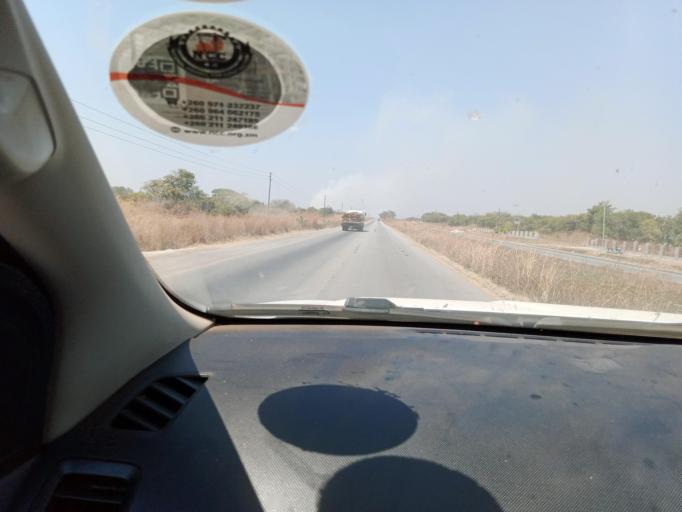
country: ZM
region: Copperbelt
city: Kitwe
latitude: -12.9152
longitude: 28.3446
